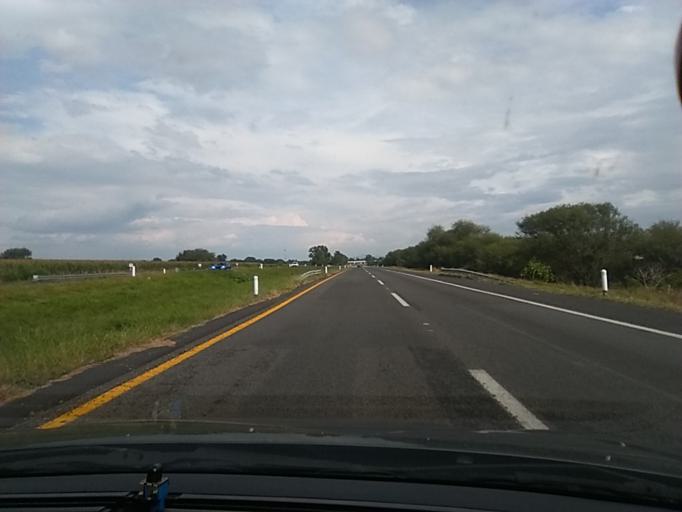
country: MX
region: Jalisco
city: La Barca
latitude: 20.3397
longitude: -102.6068
